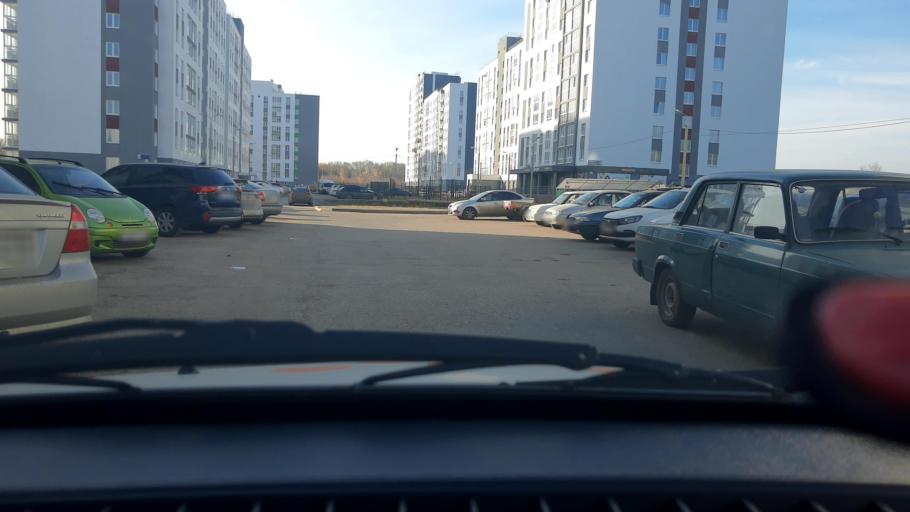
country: RU
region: Bashkortostan
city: Ufa
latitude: 54.6925
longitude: 55.9687
